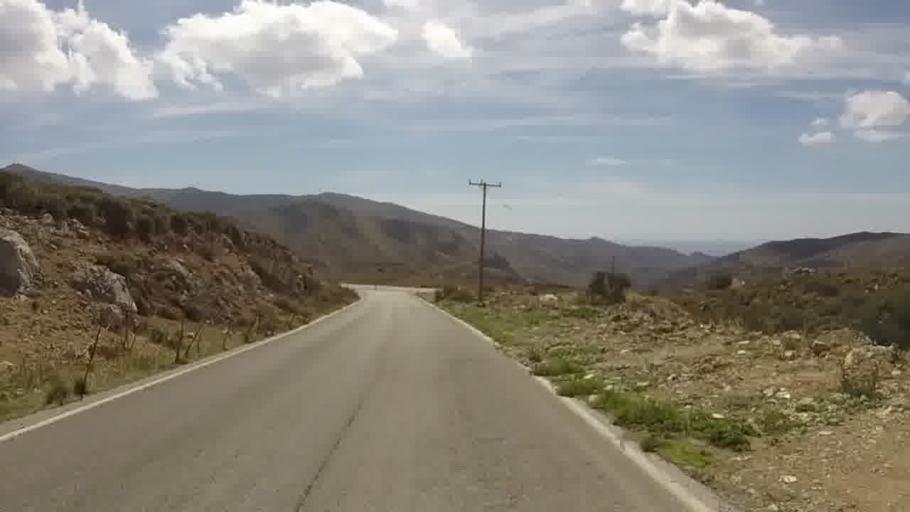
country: GR
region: Crete
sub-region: Nomos Rethymnis
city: Agia Galini
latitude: 35.1521
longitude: 24.6213
